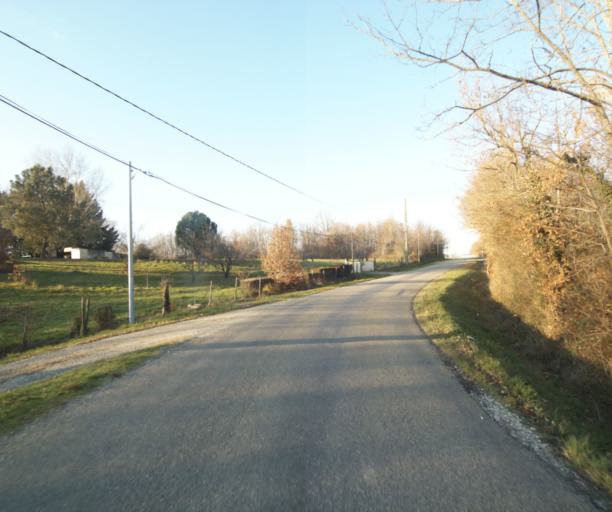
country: FR
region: Midi-Pyrenees
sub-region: Departement du Tarn-et-Garonne
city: Moissac
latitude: 44.1378
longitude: 1.1217
